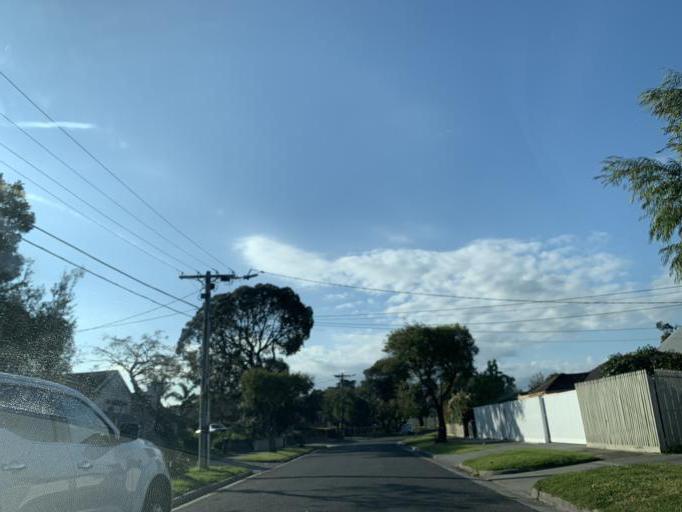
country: AU
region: Victoria
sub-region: Kingston
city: Mordialloc
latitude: -37.9932
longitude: 145.0941
